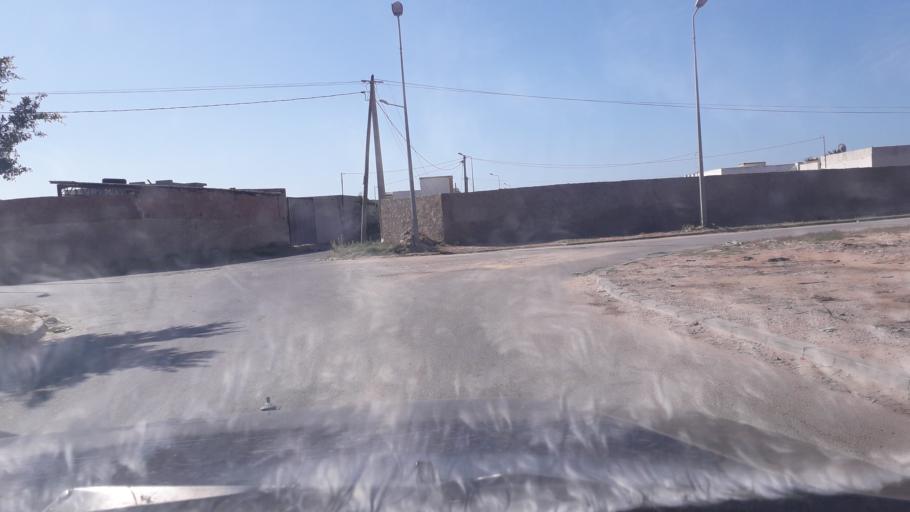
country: TN
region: Safaqis
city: Al Qarmadah
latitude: 34.8244
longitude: 10.7508
